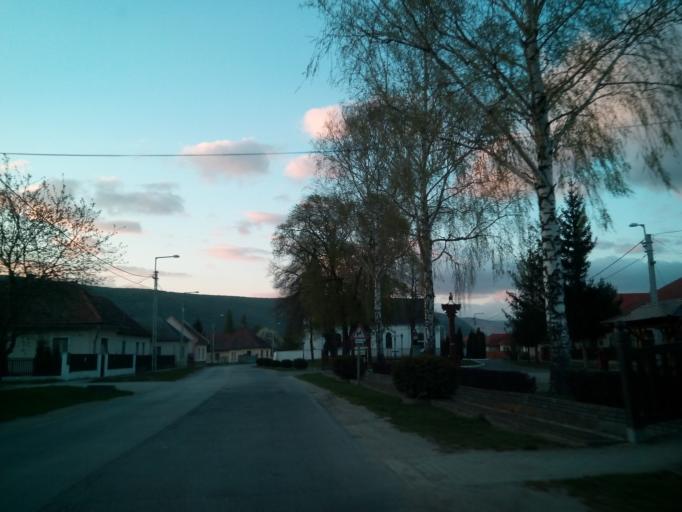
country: SK
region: Kosicky
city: Medzev
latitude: 48.5590
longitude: 20.8384
